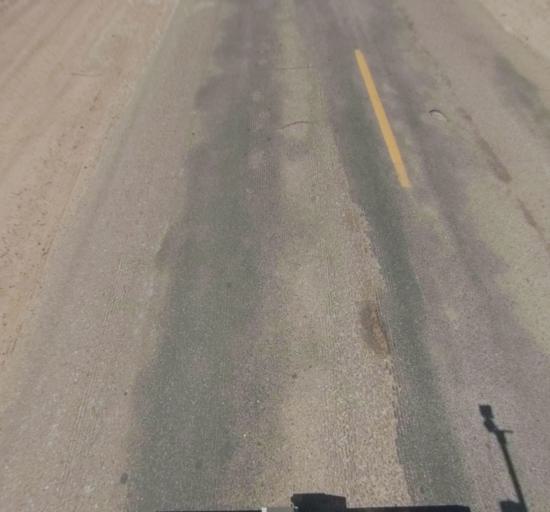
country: US
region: California
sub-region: Fresno County
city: Mendota
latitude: 36.8482
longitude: -120.2552
